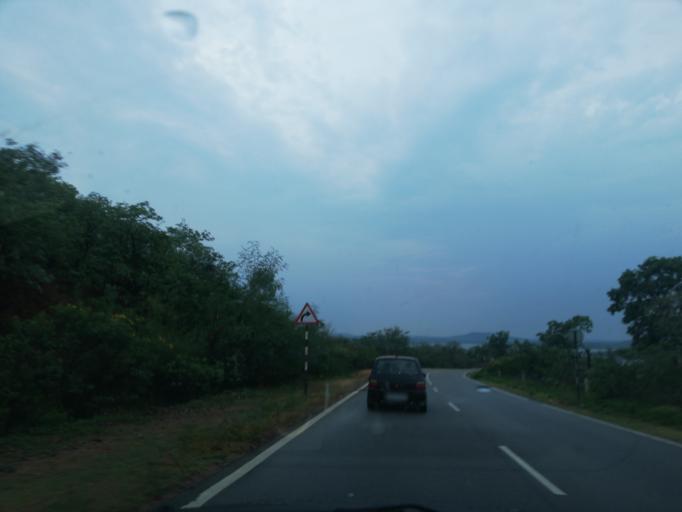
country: IN
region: Andhra Pradesh
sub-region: Guntur
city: Macherla
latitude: 16.6320
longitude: 79.2882
